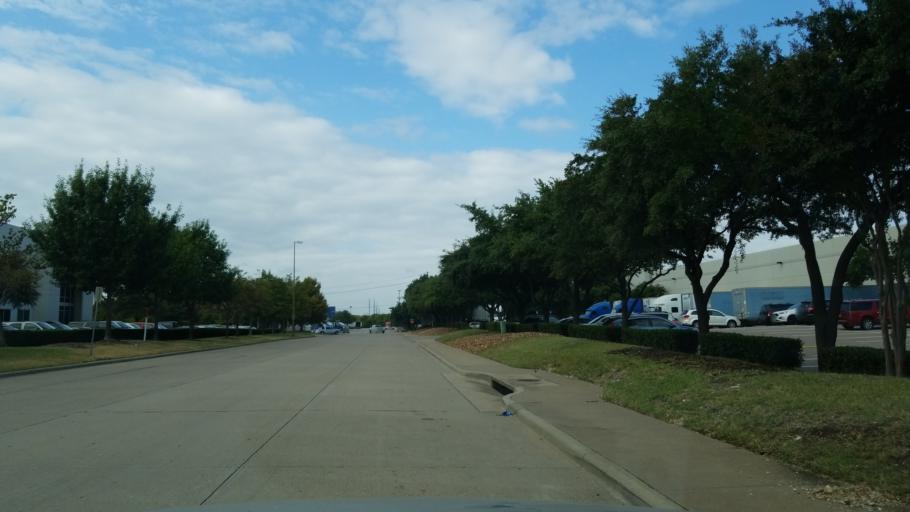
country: US
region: Texas
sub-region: Dallas County
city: Garland
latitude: 32.8892
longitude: -96.6919
